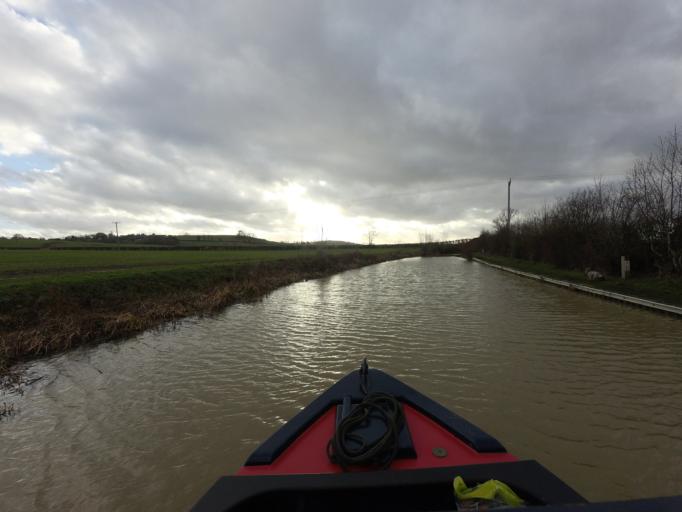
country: GB
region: England
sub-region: Warwickshire
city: Dunchurch
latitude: 52.2756
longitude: -1.2516
